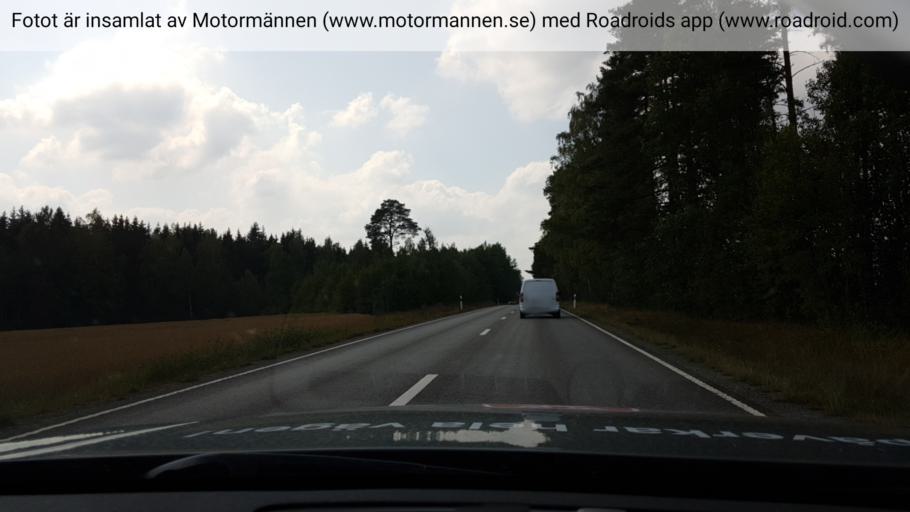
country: SE
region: Stockholm
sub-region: Sodertalje Kommun
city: Molnbo
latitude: 59.0374
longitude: 17.3707
